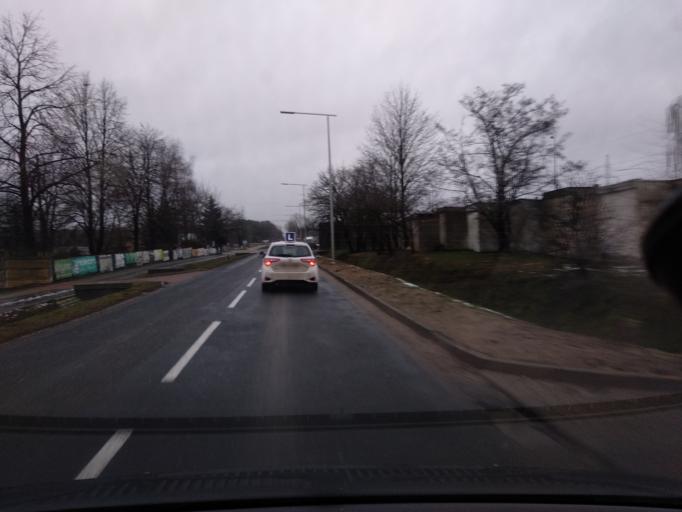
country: PL
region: Lower Silesian Voivodeship
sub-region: Powiat polkowicki
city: Polkowice
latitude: 51.5038
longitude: 16.0847
